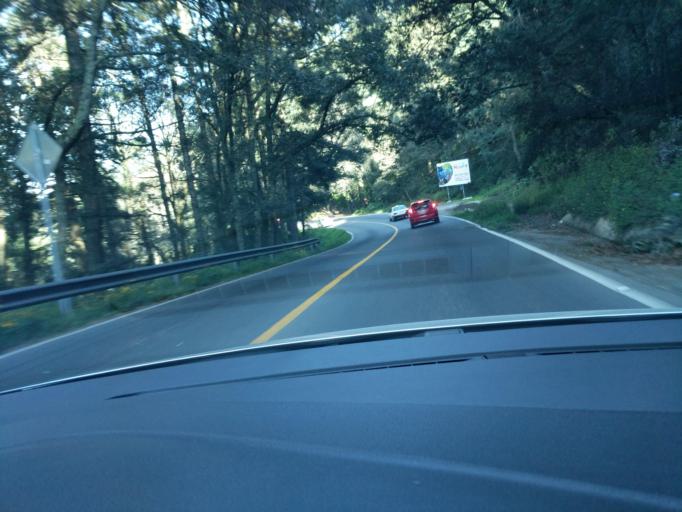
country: MX
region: Hidalgo
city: Mineral del Monte
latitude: 20.1474
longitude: -98.6836
